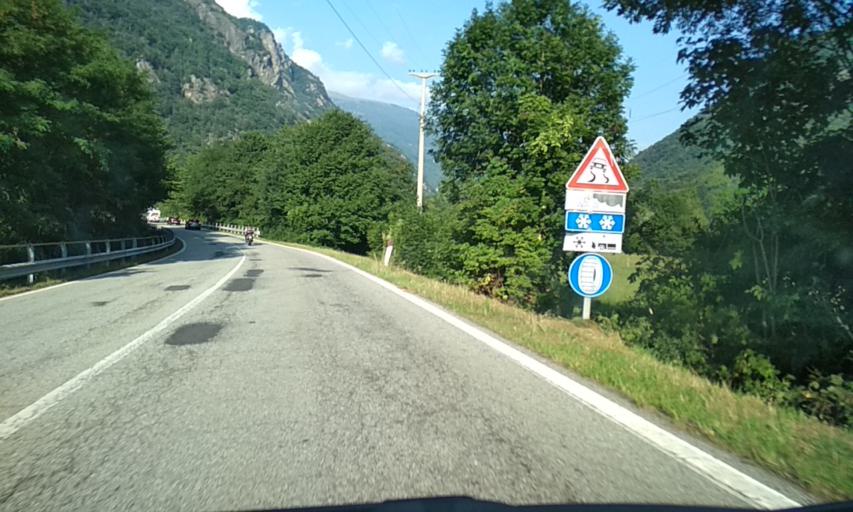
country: IT
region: Piedmont
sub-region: Provincia di Torino
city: Sparone
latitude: 45.4159
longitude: 7.5570
